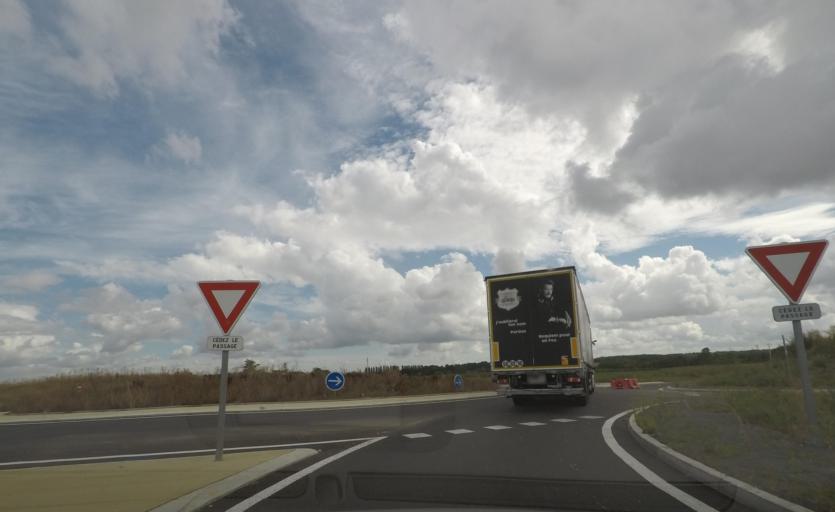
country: FR
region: Pays de la Loire
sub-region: Departement de Maine-et-Loire
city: Seiches-sur-le-Loir
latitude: 47.5662
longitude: -0.3643
